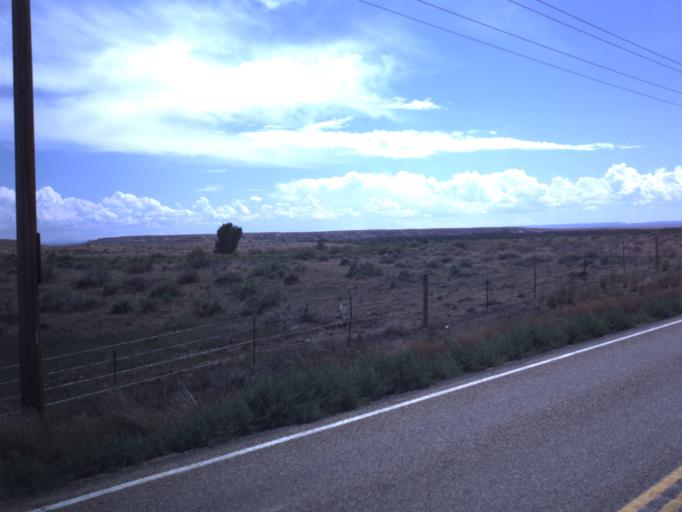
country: US
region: Utah
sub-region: Uintah County
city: Naples
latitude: 40.1347
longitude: -109.6639
